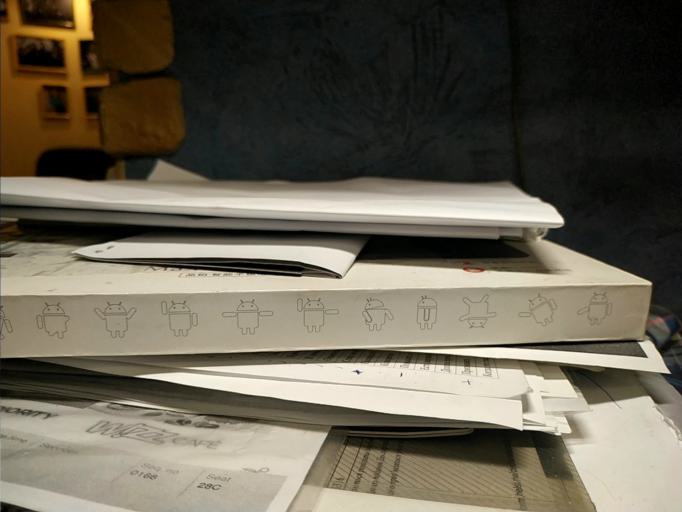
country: RU
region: Tverskaya
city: Zubtsov
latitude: 56.0858
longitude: 34.7701
